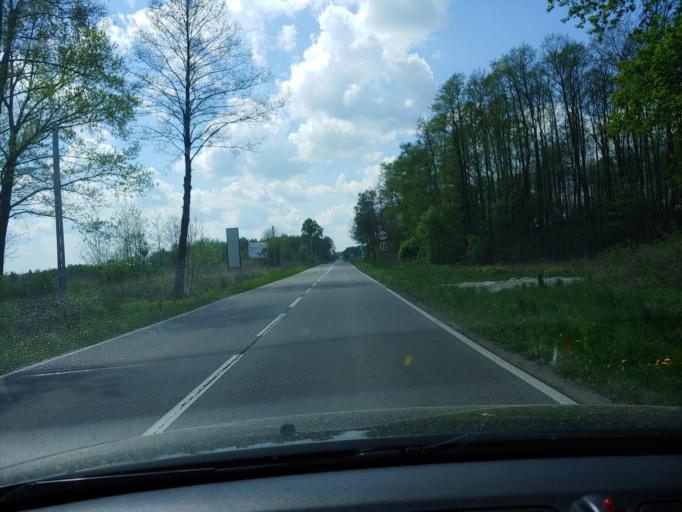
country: PL
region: Subcarpathian Voivodeship
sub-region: Powiat mielecki
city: Wadowice Gorne
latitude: 50.2493
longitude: 21.3142
